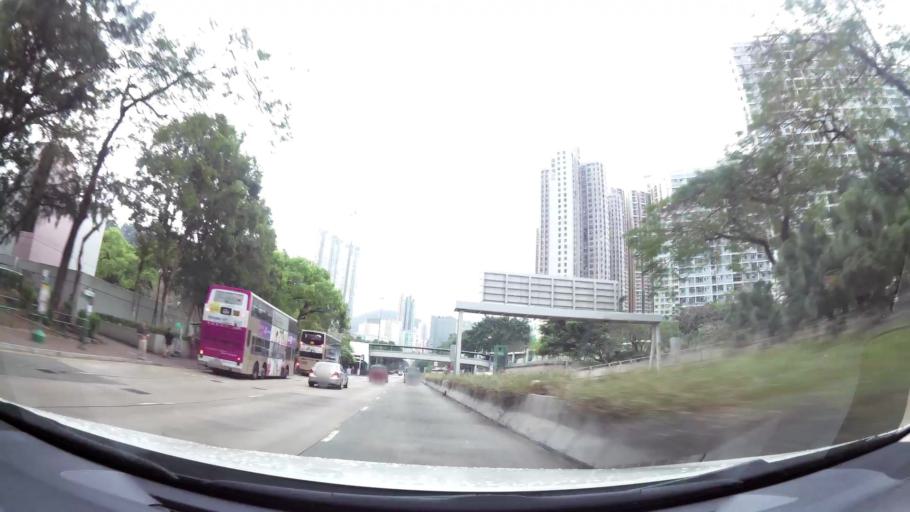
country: HK
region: Tsuen Wan
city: Tsuen Wan
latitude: 22.3704
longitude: 114.1235
